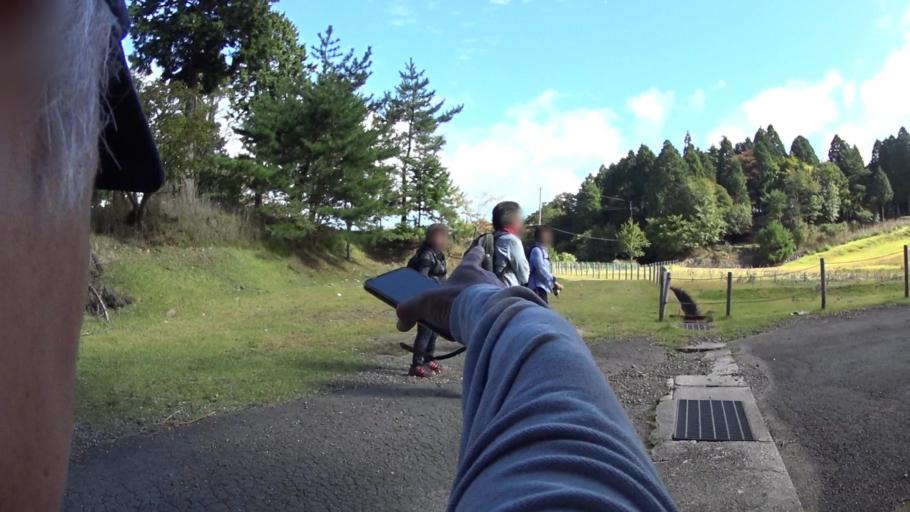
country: JP
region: Shiga Prefecture
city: Otsu-shi
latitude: 35.0664
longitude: 135.8262
